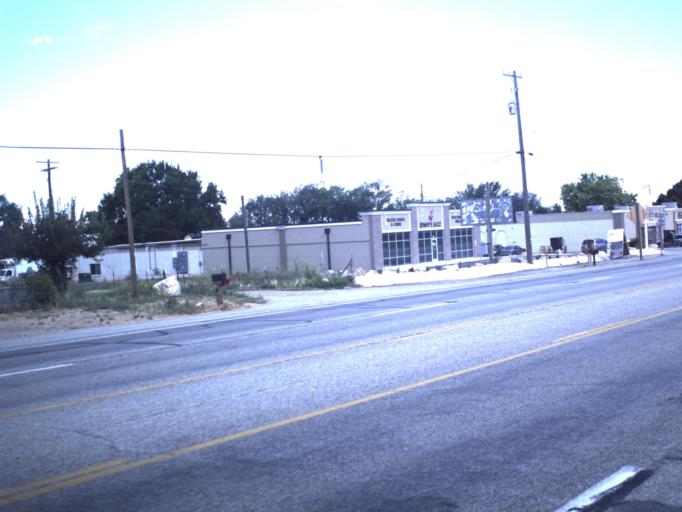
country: US
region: Utah
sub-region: Box Elder County
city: Willard
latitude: 41.4235
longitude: -112.0357
